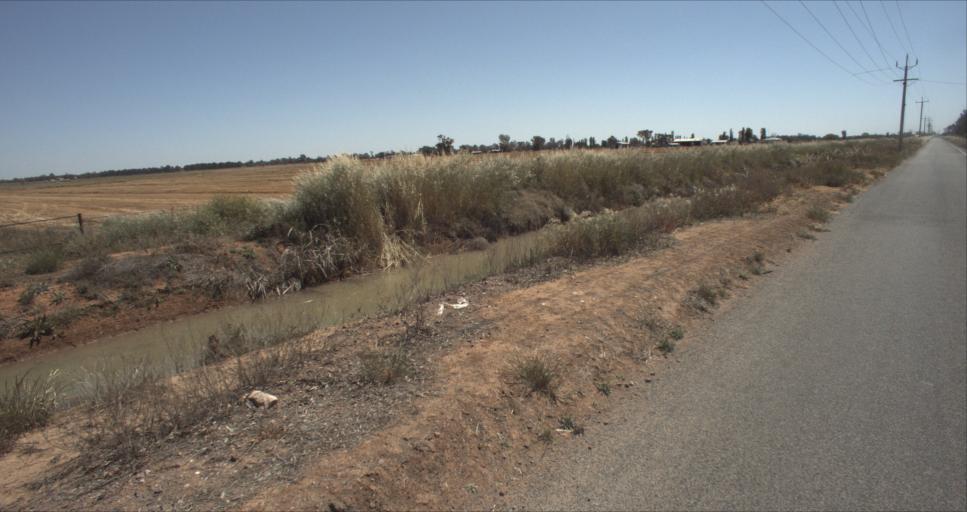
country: AU
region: New South Wales
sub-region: Leeton
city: Leeton
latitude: -34.5150
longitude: 146.4322
